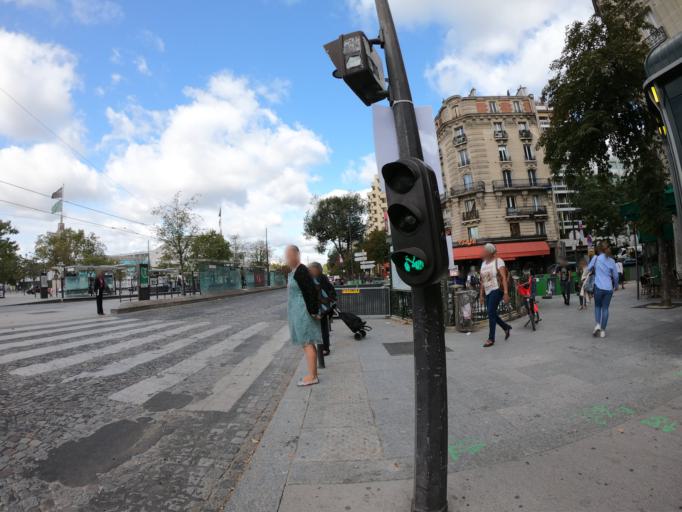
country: FR
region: Ile-de-France
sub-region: Departement des Hauts-de-Seine
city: Vanves
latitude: 48.8326
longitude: 2.2887
